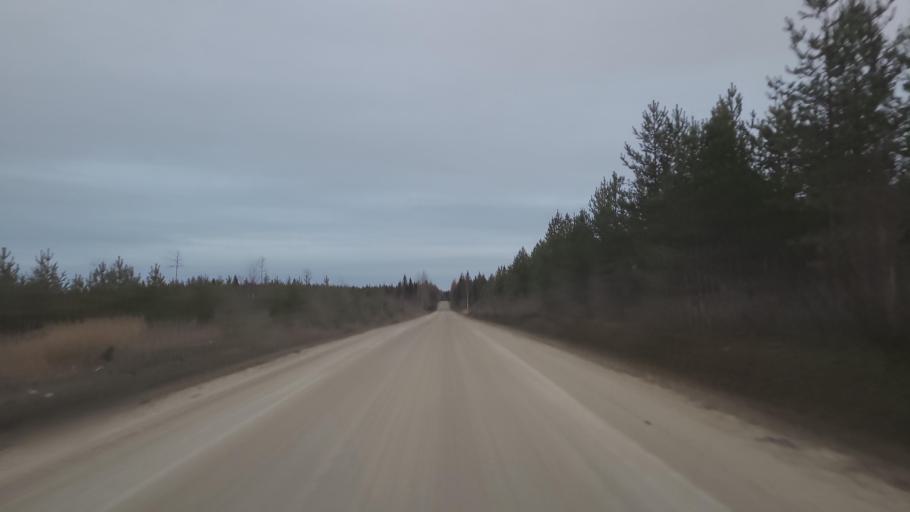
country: FI
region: Lapland
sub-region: Kemi-Tornio
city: Tervola
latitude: 66.0721
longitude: 24.8677
